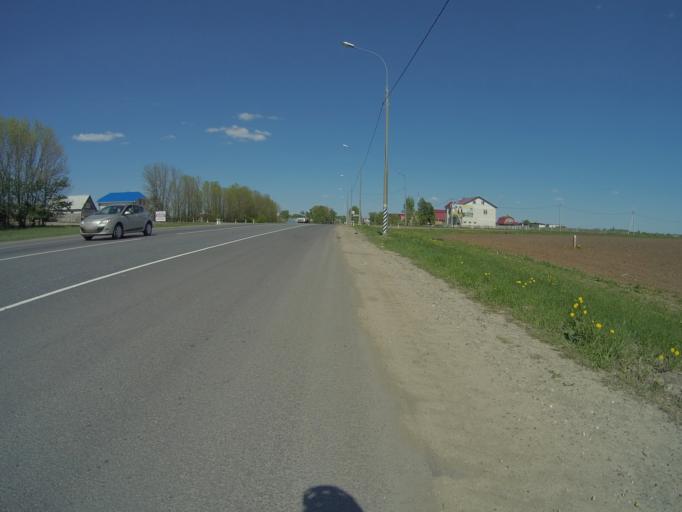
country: RU
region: Vladimir
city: Suzdal'
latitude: 56.3118
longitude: 40.4709
